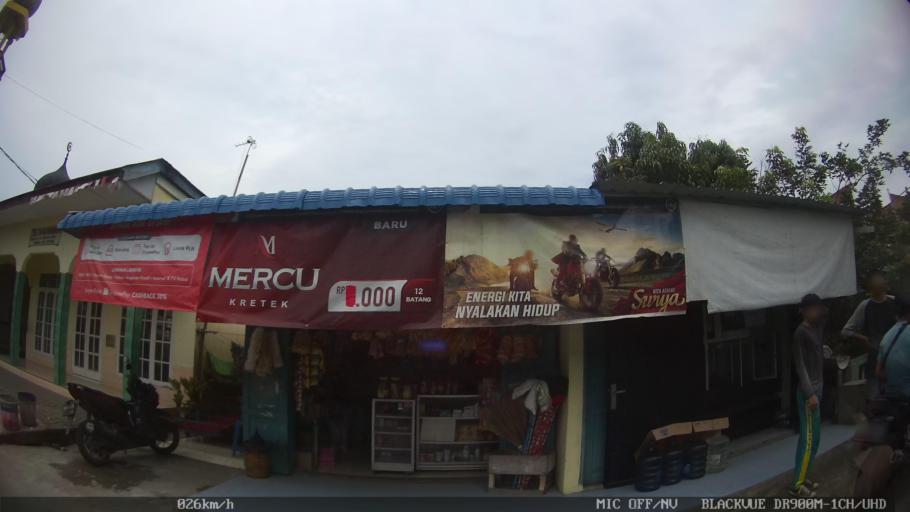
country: ID
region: North Sumatra
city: Sunggal
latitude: 3.6007
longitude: 98.5540
